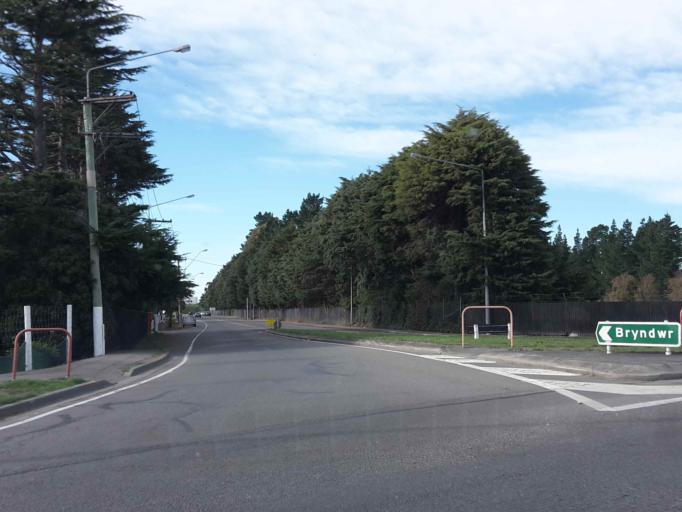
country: NZ
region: Canterbury
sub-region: Christchurch City
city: Christchurch
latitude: -43.4862
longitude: 172.5539
